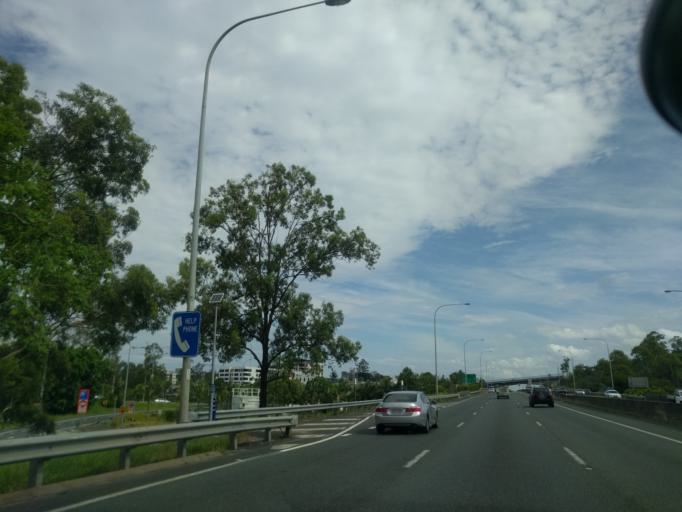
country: AU
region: Queensland
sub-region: Brisbane
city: Woolloongabba
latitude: -27.4842
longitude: 153.0315
